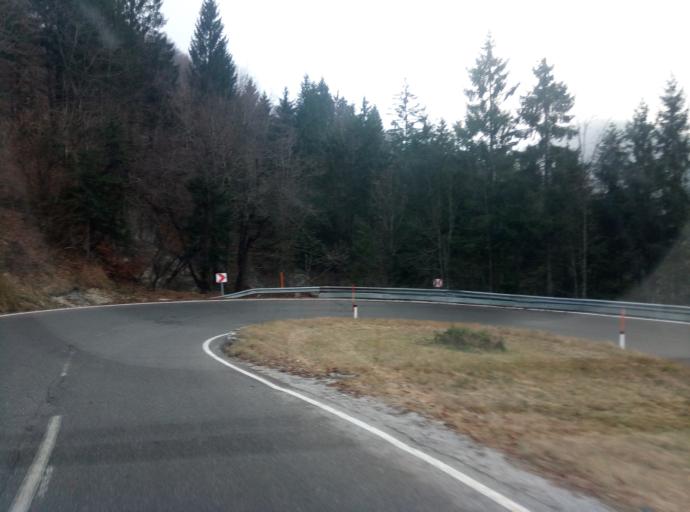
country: SI
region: Idrija
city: Idrija
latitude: 45.9217
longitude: 14.0462
